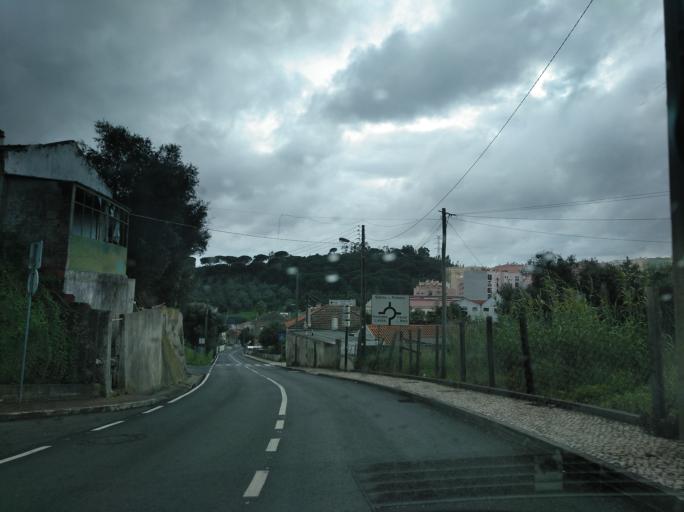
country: PT
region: Lisbon
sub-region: Odivelas
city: Famoes
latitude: 38.7828
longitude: -9.2074
